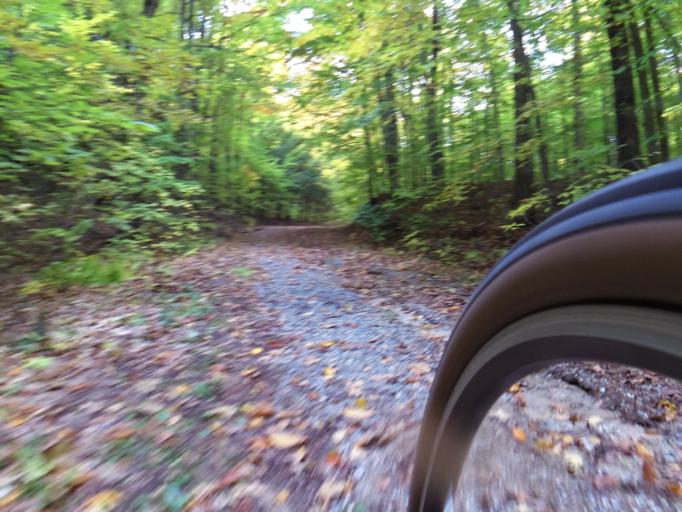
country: CA
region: Quebec
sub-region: Outaouais
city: Wakefield
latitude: 45.6011
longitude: -76.0616
